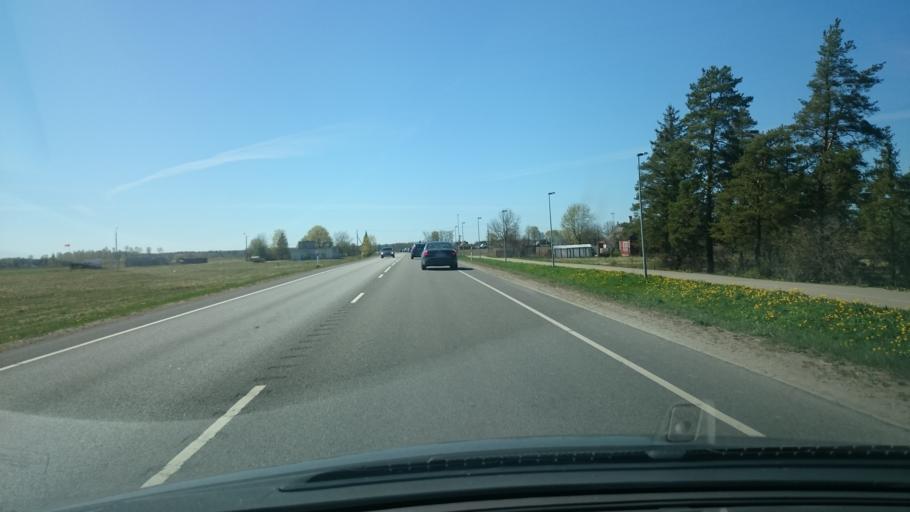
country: EE
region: Ida-Virumaa
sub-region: Narva linn
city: Narva
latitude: 59.3896
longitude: 28.1167
